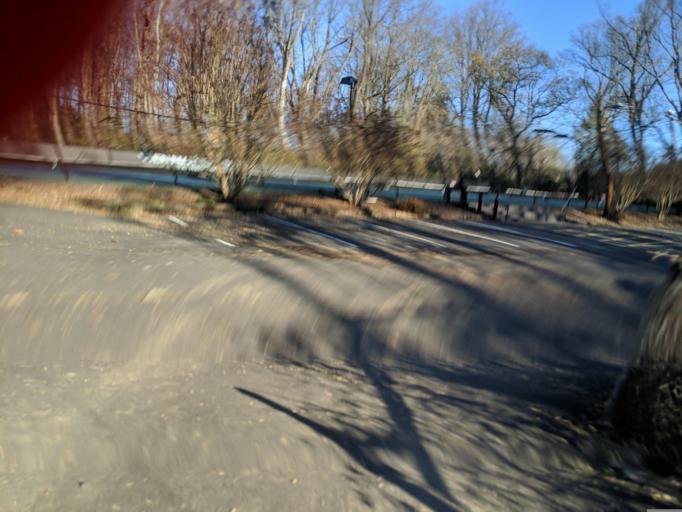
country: US
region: Virginia
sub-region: Fairfax County
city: Vienna
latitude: 38.8907
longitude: -77.2533
